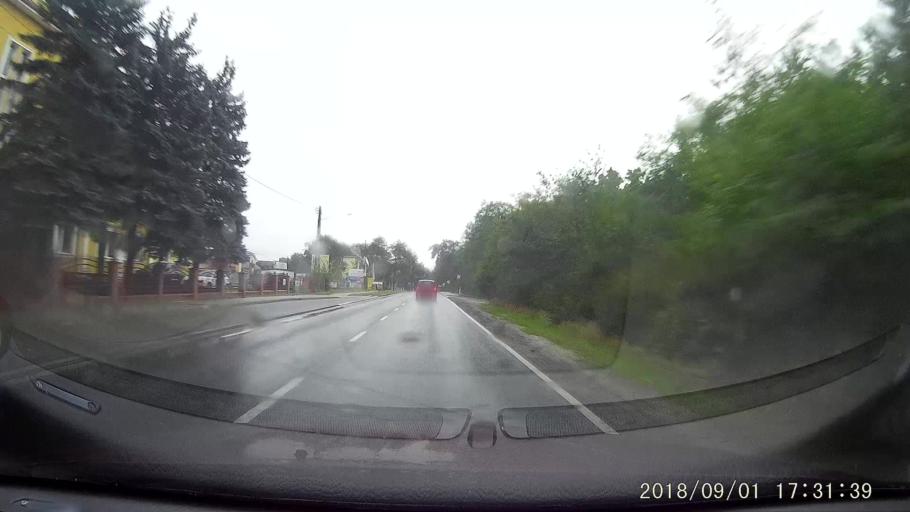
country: PL
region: Lubusz
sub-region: Powiat zaganski
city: Zagan
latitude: 51.6315
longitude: 15.3244
